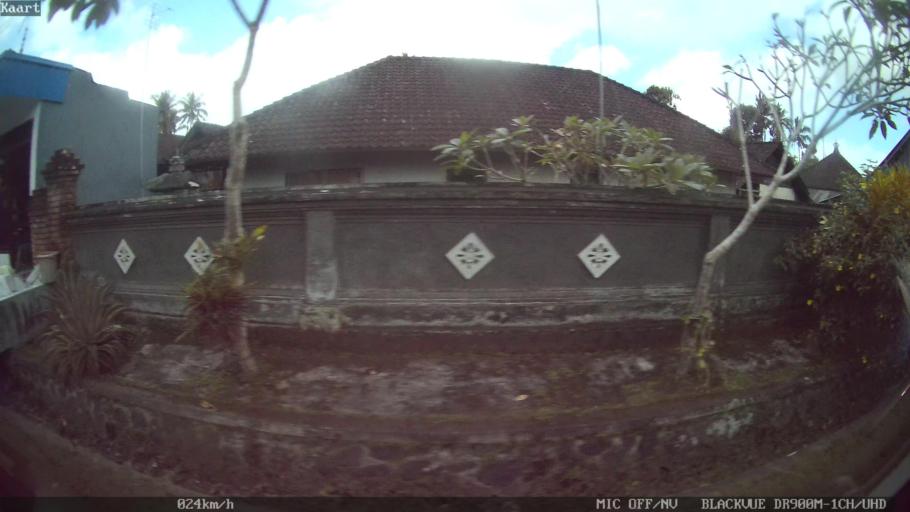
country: ID
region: Bali
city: Banjar Petak
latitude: -8.4438
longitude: 115.3191
